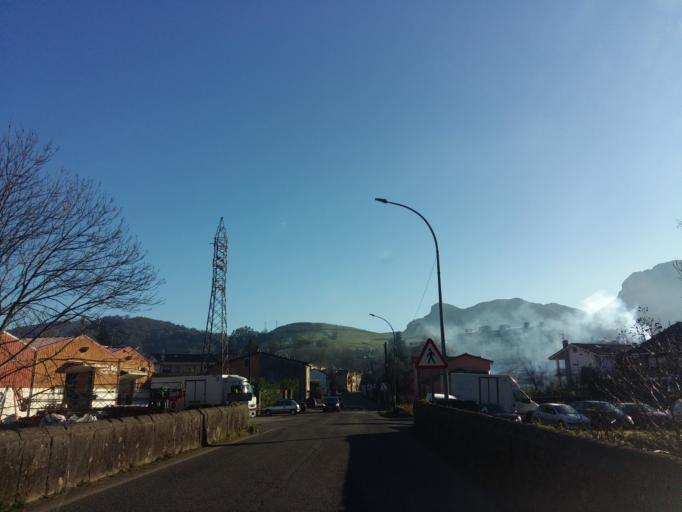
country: ES
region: Cantabria
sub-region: Provincia de Cantabria
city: Ramales de la Victoria
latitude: 43.2614
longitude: -3.4699
